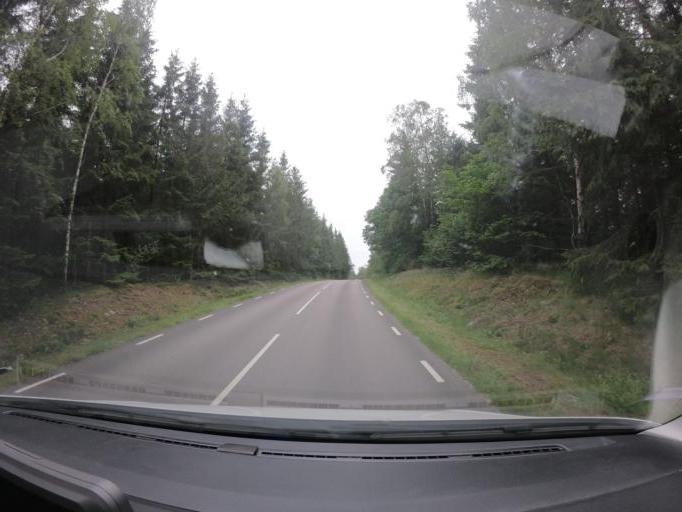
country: SE
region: Skane
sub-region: Perstorps Kommun
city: Perstorp
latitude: 56.1034
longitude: 13.4126
